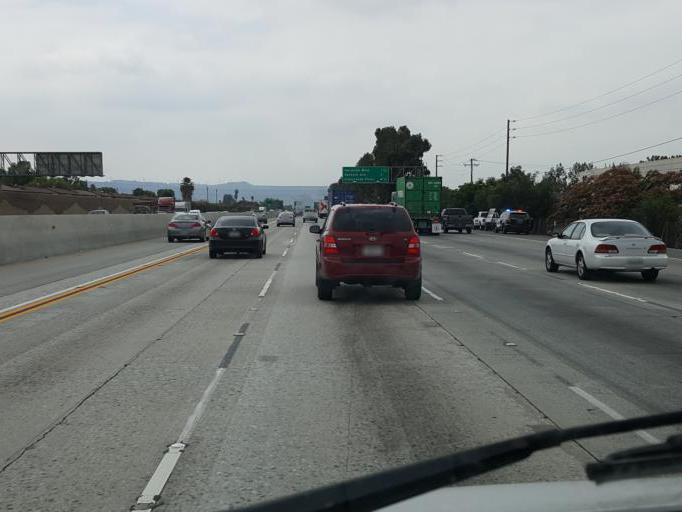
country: US
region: California
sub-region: Los Angeles County
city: La Puente
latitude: 33.9988
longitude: -117.9377
